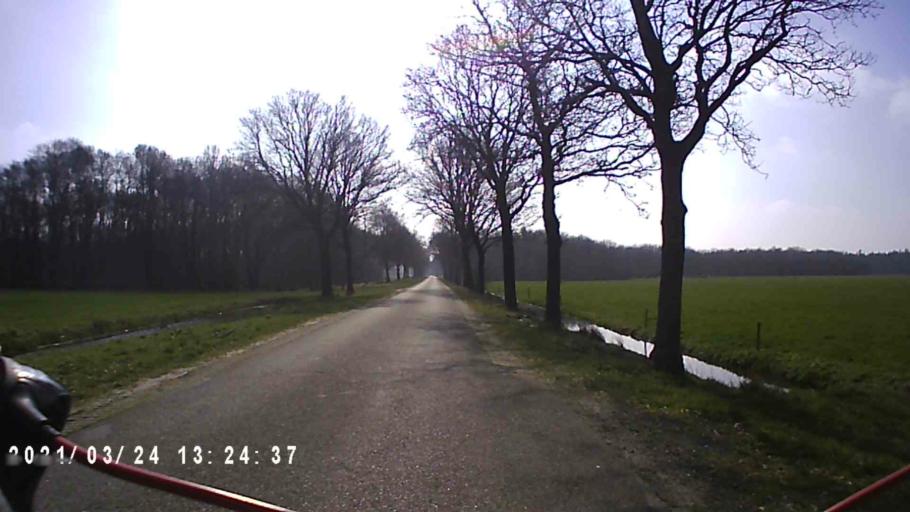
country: NL
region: Groningen
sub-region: Gemeente Grootegast
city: Grootegast
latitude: 53.0961
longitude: 6.2775
